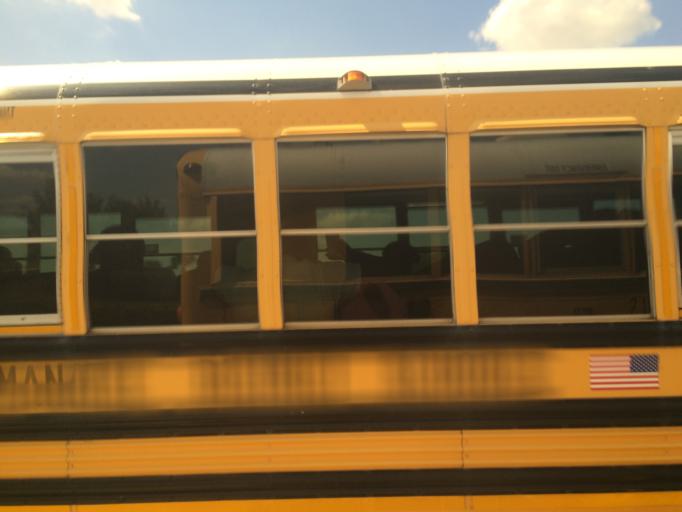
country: US
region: Florida
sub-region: Sarasota County
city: The Meadows
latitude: 27.4563
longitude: -82.4319
